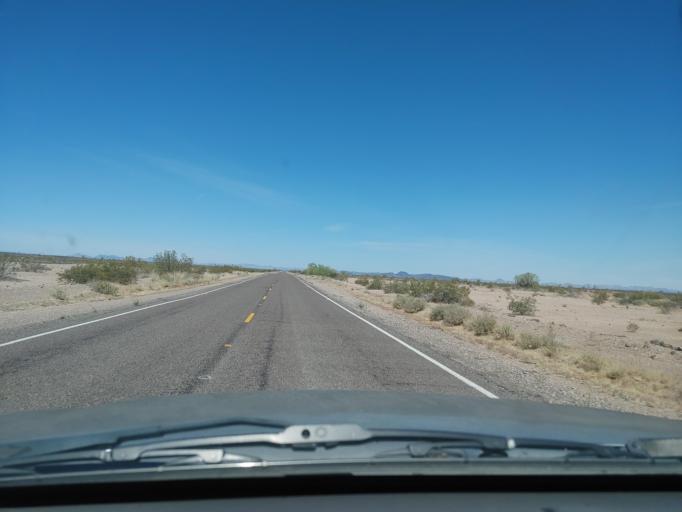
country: US
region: Arizona
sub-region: Maricopa County
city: Gila Bend
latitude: 32.8857
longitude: -113.2338
